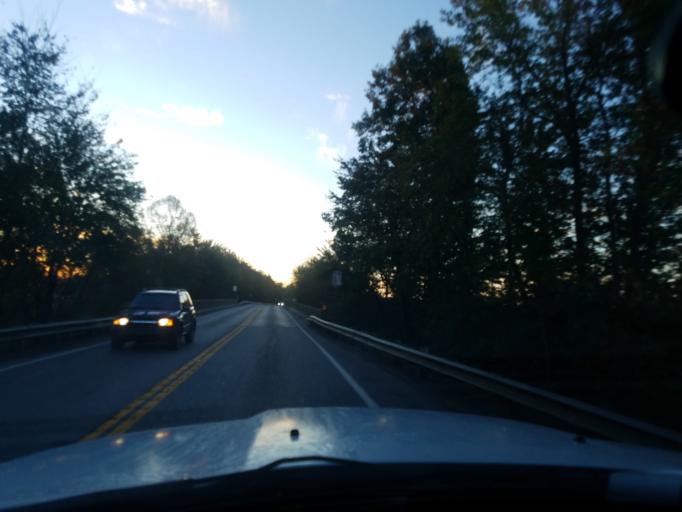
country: US
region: Kentucky
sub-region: Laurel County
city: London
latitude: 37.0639
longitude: -84.0563
